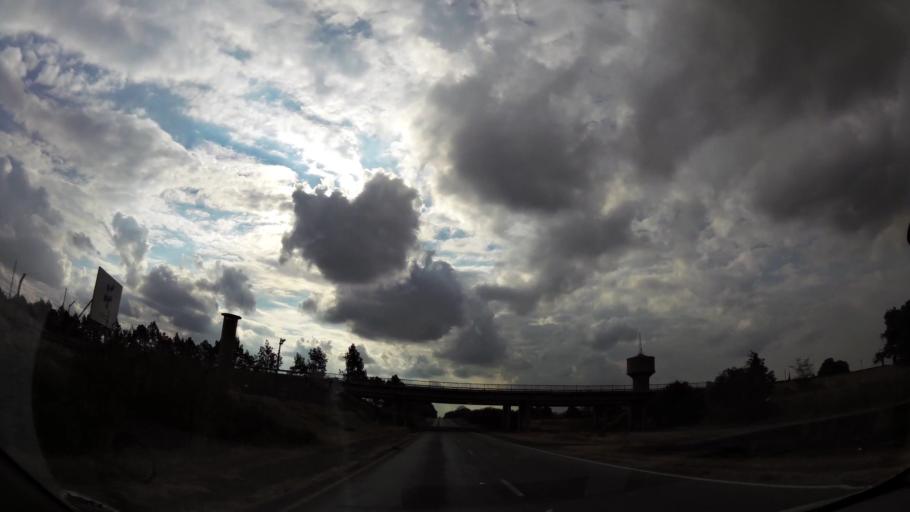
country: ZA
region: Orange Free State
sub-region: Fezile Dabi District Municipality
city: Sasolburg
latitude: -26.8180
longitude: 27.8432
